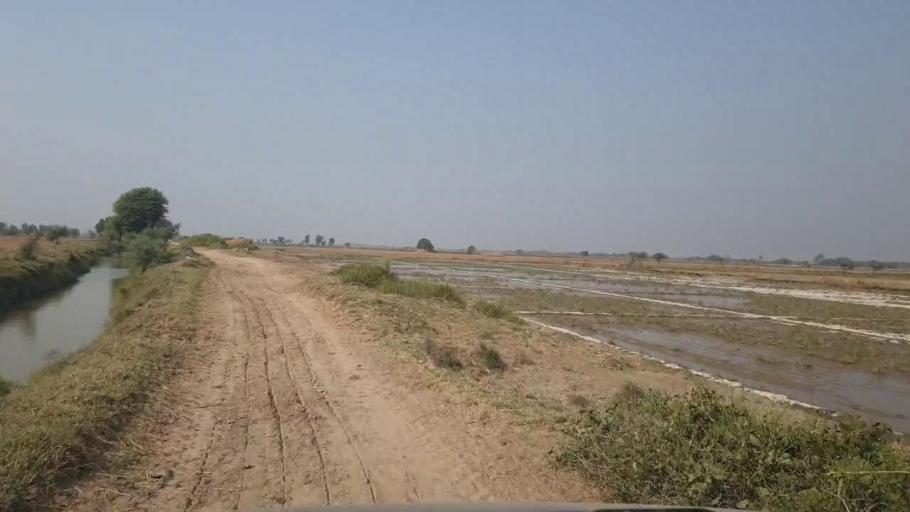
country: PK
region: Sindh
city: Tando Muhammad Khan
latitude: 25.0699
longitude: 68.3574
